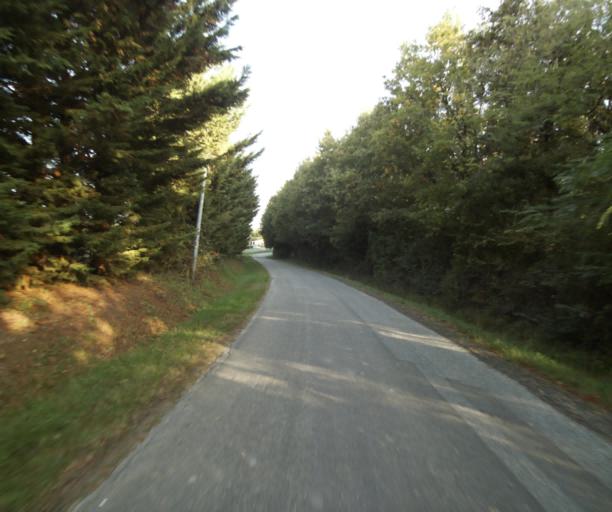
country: FR
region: Midi-Pyrenees
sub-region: Departement du Tarn-et-Garonne
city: Nohic
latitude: 43.9113
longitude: 1.4801
